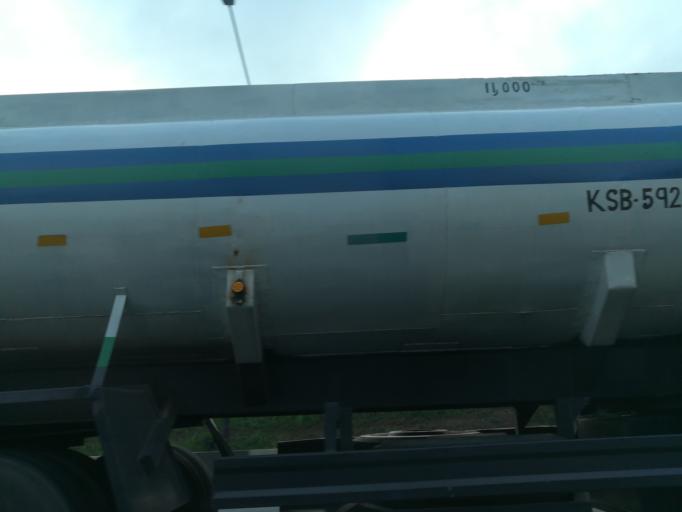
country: NG
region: Lagos
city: Ikeja
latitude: 6.6250
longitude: 3.3640
